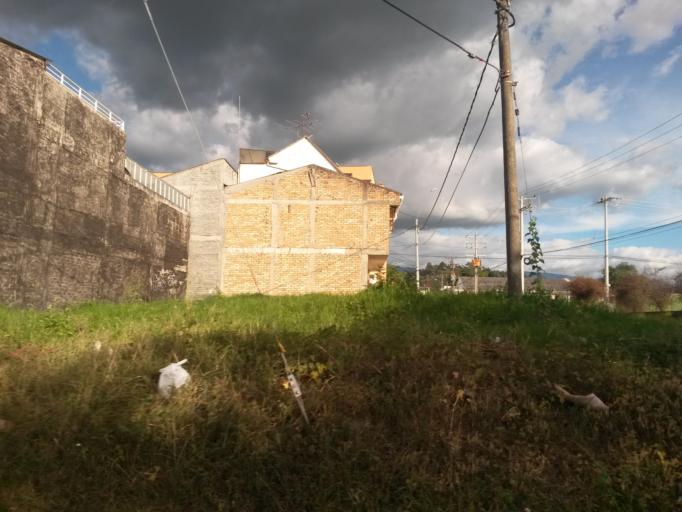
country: CO
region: Cauca
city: Popayan
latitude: 2.4561
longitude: -76.5995
